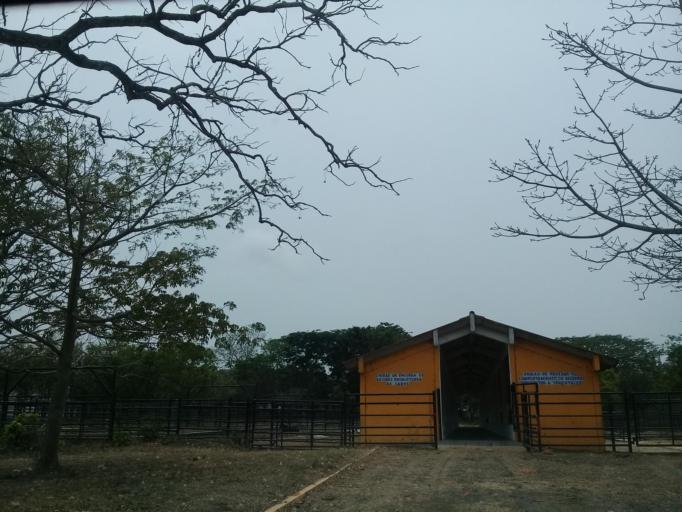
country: MX
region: Veracruz
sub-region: Veracruz
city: Lomas de Rio Medio Cuatro
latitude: 19.1736
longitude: -96.2103
